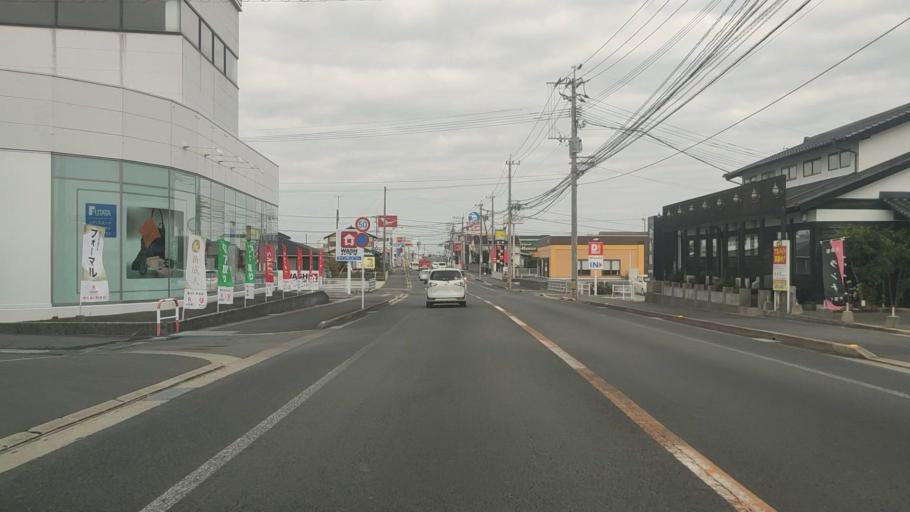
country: JP
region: Nagasaki
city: Shimabara
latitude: 32.8027
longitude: 130.3636
